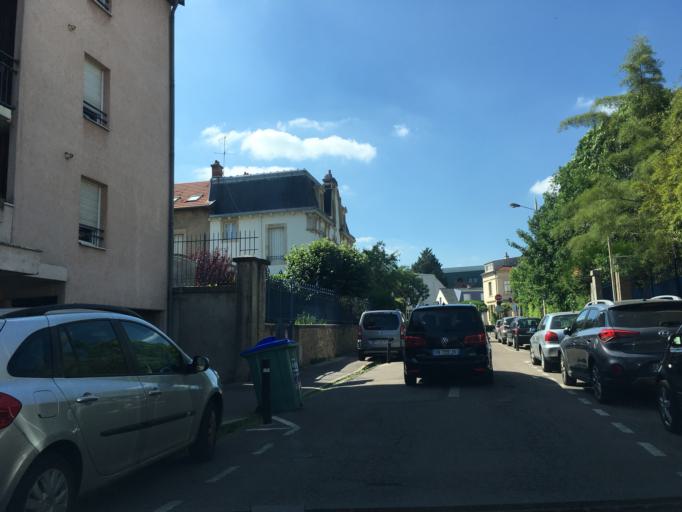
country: FR
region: Lorraine
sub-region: Departement de Meurthe-et-Moselle
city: Nancy
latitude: 48.6708
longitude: 6.1722
